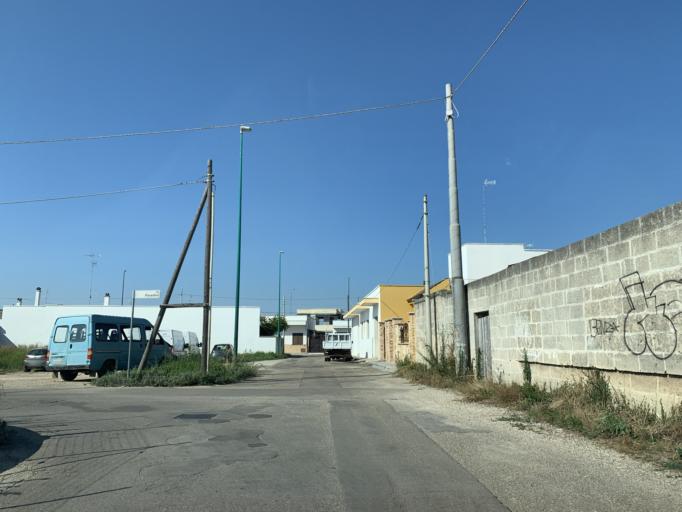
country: IT
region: Apulia
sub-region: Provincia di Lecce
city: Copertino
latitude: 40.2665
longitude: 18.0377
